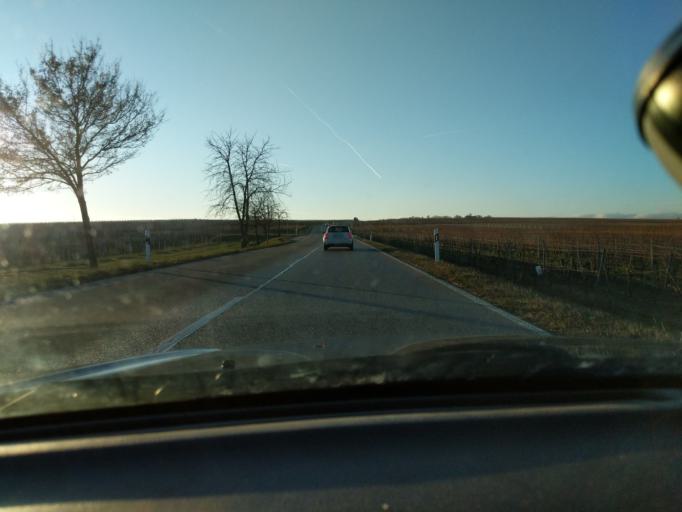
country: DE
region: Rheinland-Pfalz
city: Dackenheim
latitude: 49.5210
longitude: 8.1785
